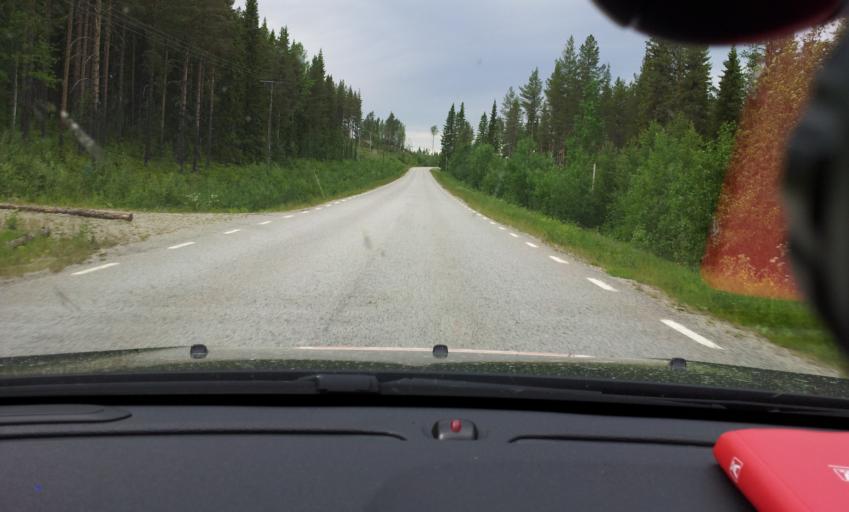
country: SE
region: Jaemtland
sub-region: Bergs Kommun
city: Hoverberg
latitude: 62.6674
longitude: 14.7267
